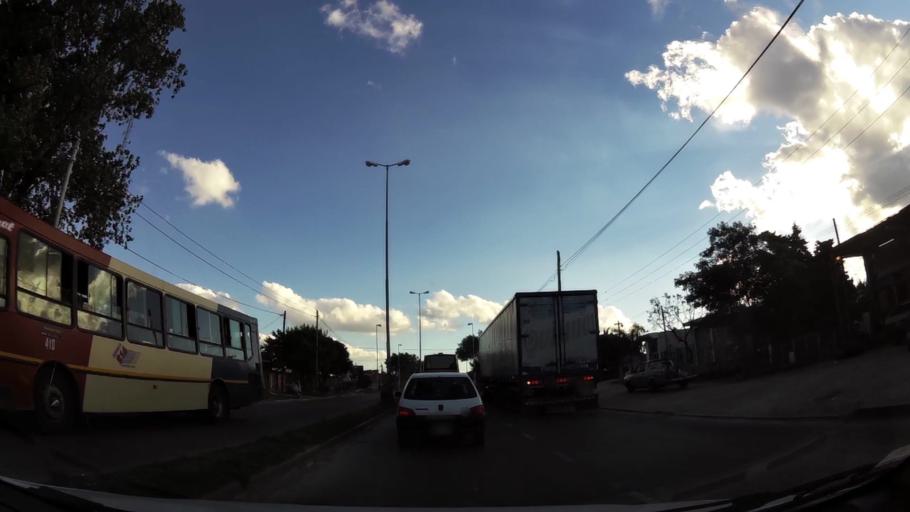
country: AR
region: Buenos Aires
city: Ituzaingo
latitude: -34.6973
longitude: -58.6384
